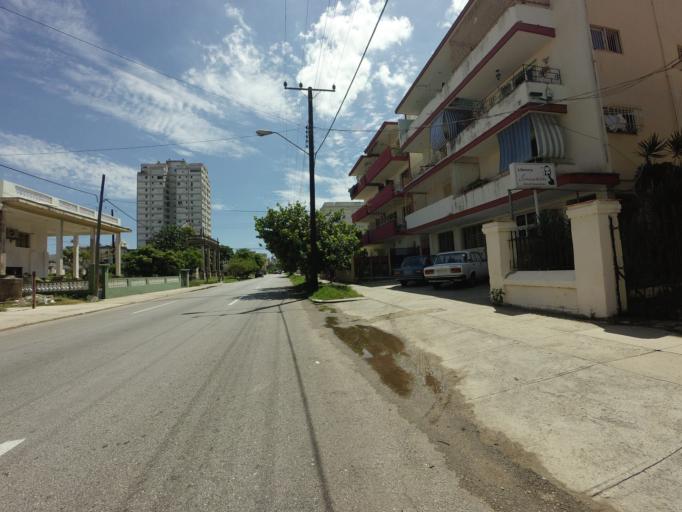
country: CU
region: La Habana
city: Havana
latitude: 23.1370
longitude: -82.4016
